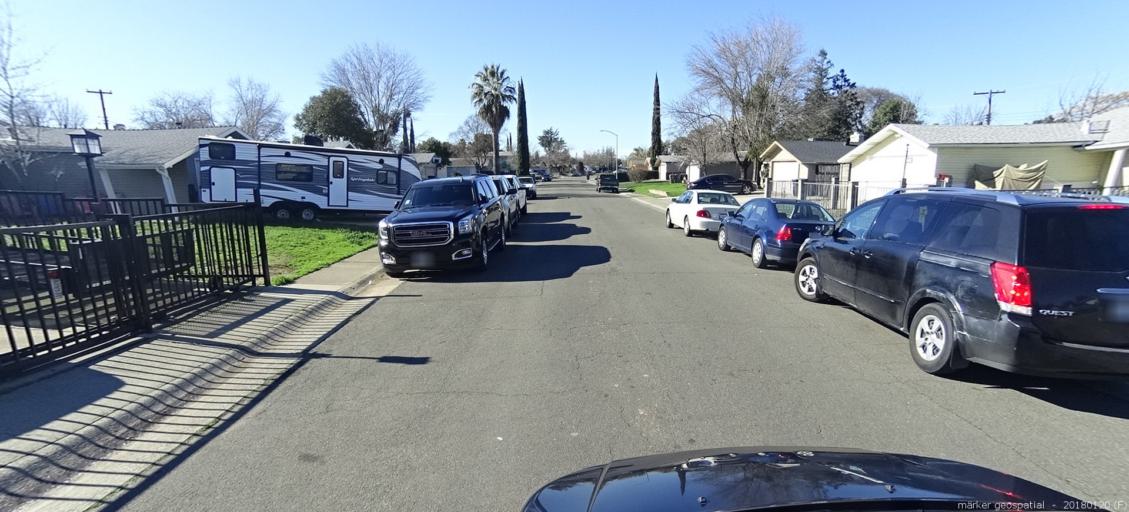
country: US
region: California
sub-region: Sacramento County
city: La Riviera
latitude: 38.5644
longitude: -121.3246
